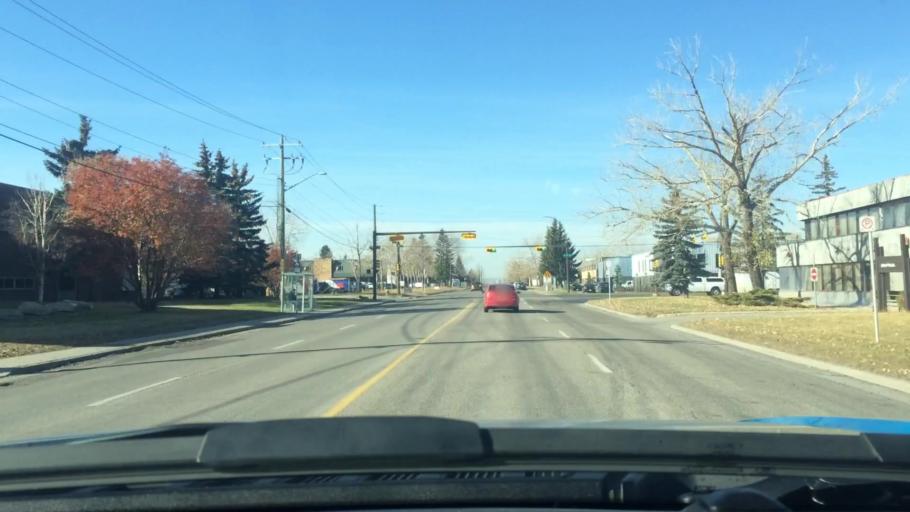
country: CA
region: Alberta
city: Calgary
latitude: 51.0769
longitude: -114.0104
